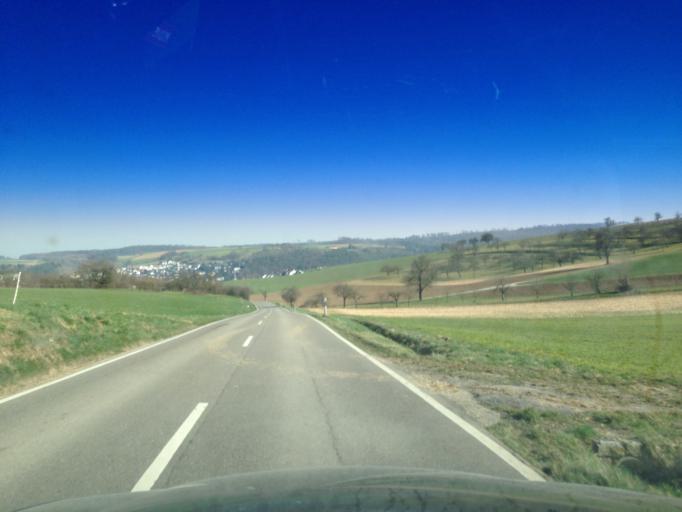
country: DE
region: Baden-Wuerttemberg
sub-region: Regierungsbezirk Stuttgart
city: Eberdingen
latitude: 48.8842
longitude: 8.9499
